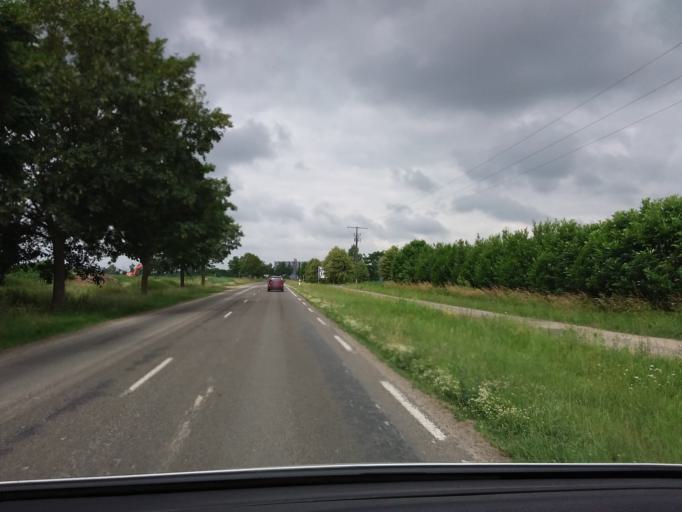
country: FR
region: Picardie
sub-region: Departement de l'Aisne
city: Bucy-le-Long
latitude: 49.3899
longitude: 3.3830
